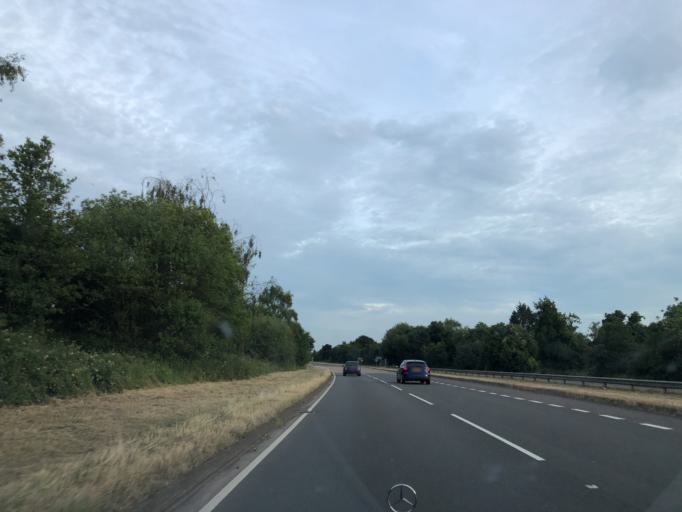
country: GB
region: England
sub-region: Solihull
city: Hampton in Arden
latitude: 52.4217
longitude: -1.6783
